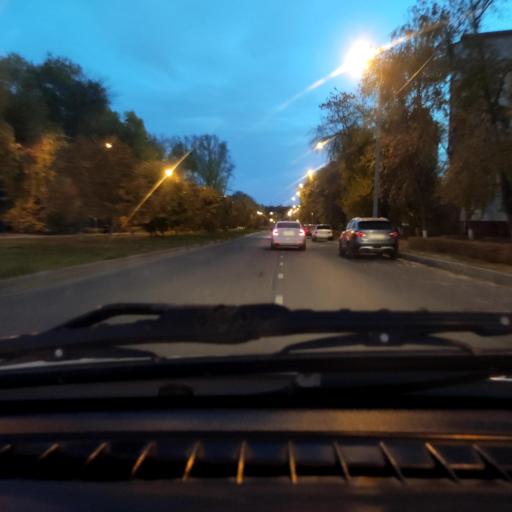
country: RU
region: Samara
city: Tol'yatti
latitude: 53.5029
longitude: 49.4006
